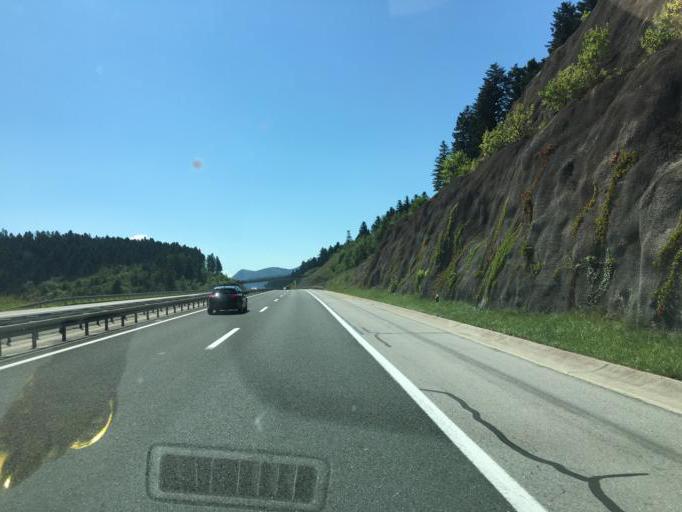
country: HR
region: Licko-Senjska
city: Otocac
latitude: 44.8521
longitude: 15.2279
